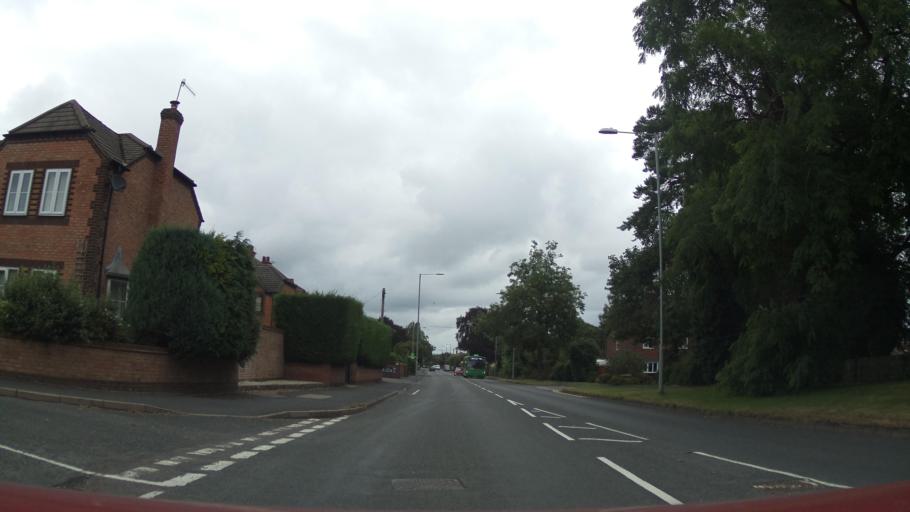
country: GB
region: England
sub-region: Worcestershire
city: Droitwich
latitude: 52.2561
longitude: -2.1575
